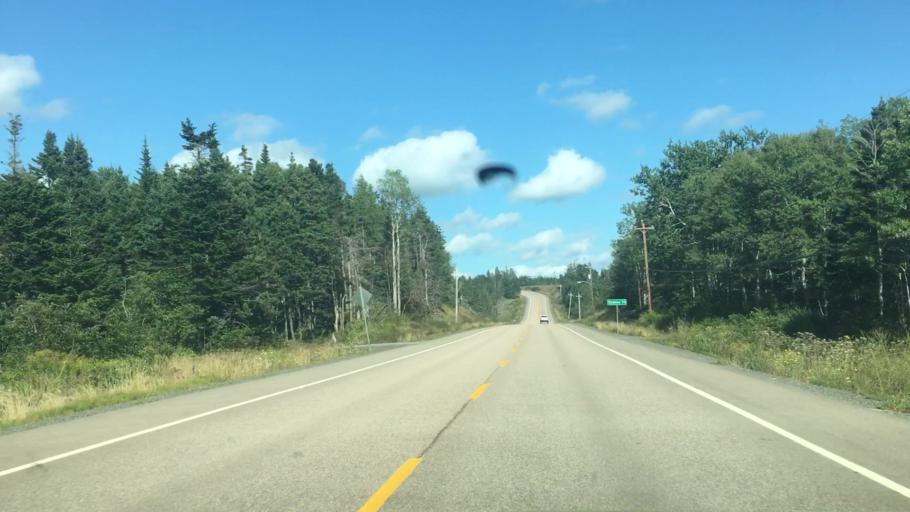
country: CA
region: Nova Scotia
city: Princeville
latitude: 45.6927
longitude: -60.7440
